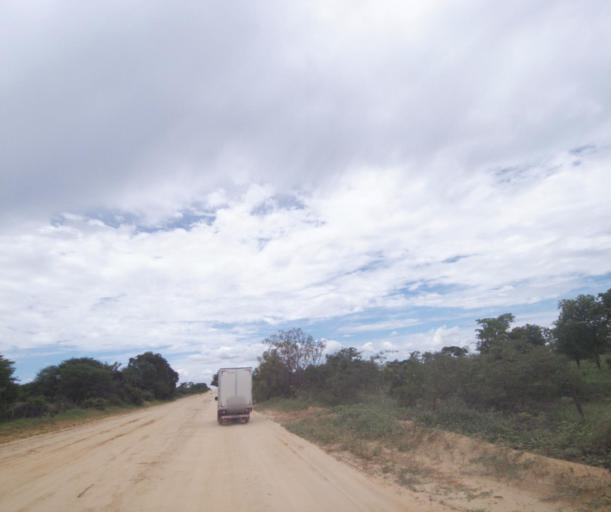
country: BR
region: Bahia
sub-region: Carinhanha
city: Carinhanha
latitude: -14.2821
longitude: -43.7914
